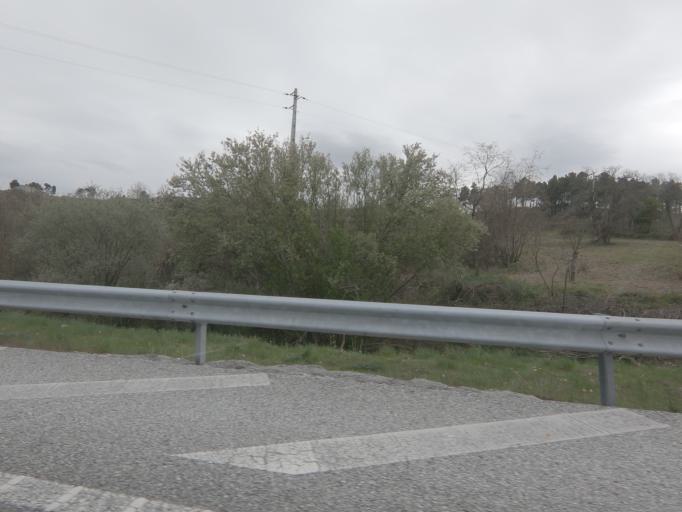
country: PT
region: Guarda
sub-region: Guarda
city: Guarda
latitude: 40.5860
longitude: -7.2657
